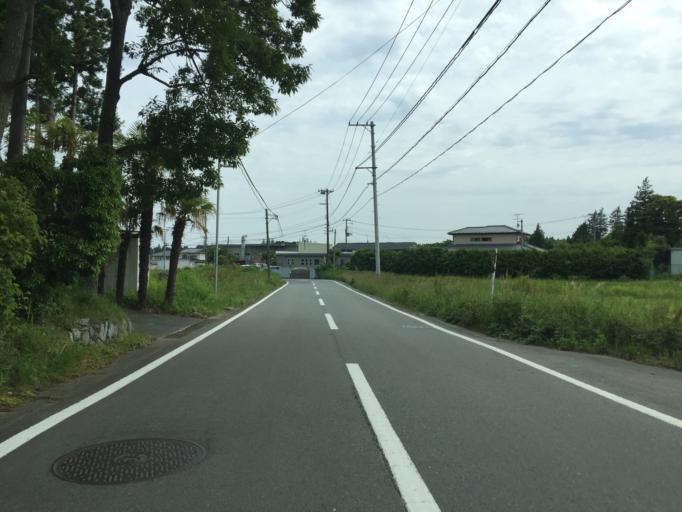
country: JP
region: Fukushima
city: Namie
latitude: 37.2954
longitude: 140.9994
